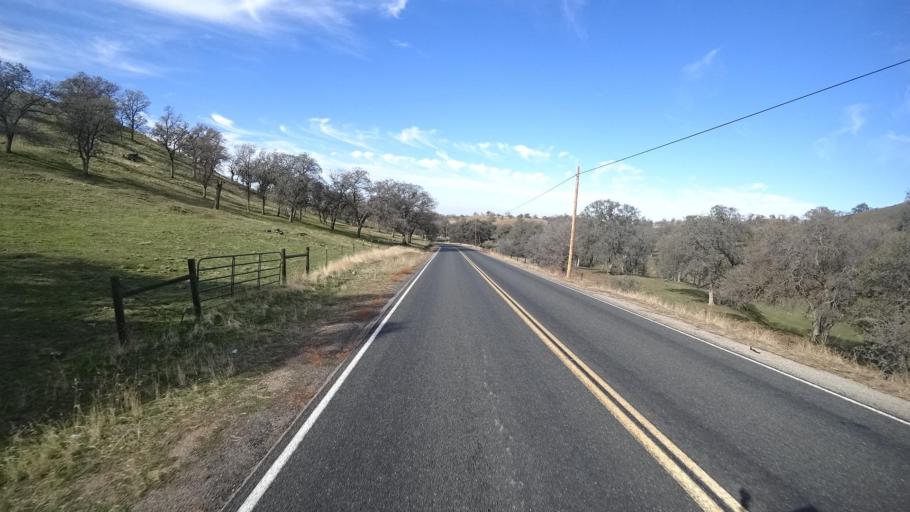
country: US
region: California
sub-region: Kern County
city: Alta Sierra
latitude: 35.6288
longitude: -118.8150
